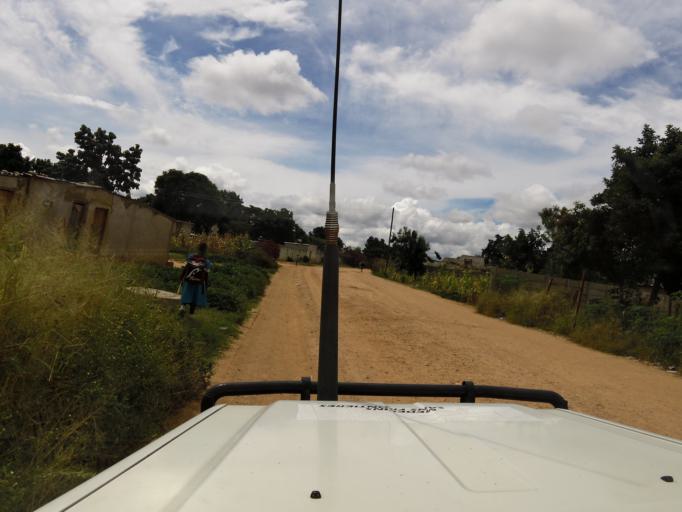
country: ZW
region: Harare
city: Epworth
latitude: -17.8937
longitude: 31.1393
